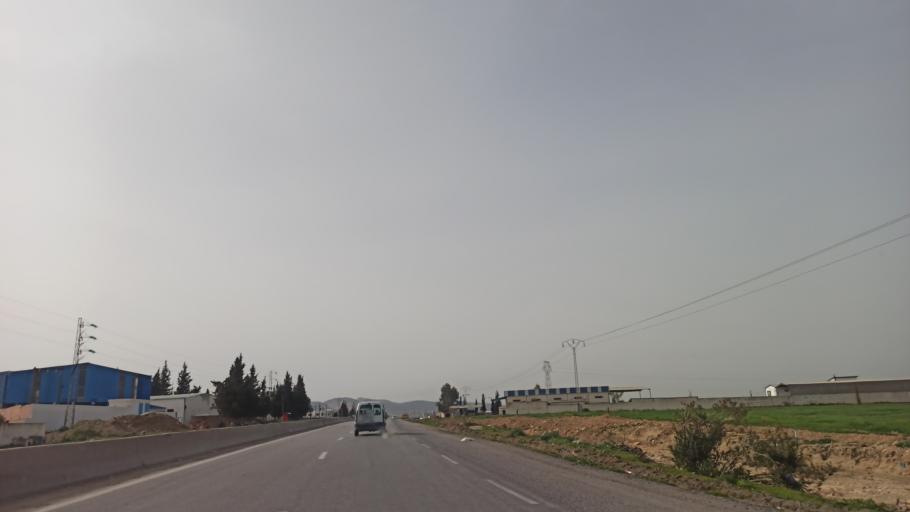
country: TN
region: Tunis
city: La Mohammedia
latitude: 36.5758
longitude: 10.0907
